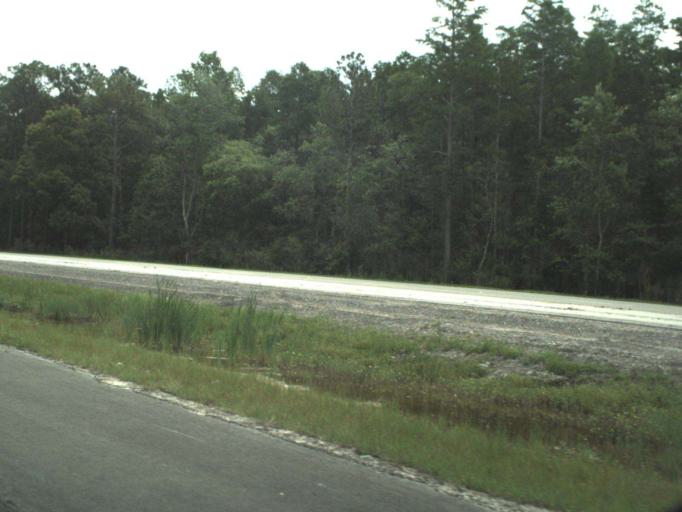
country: US
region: Florida
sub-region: Volusia County
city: Lake Helen
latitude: 29.0453
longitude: -81.2056
